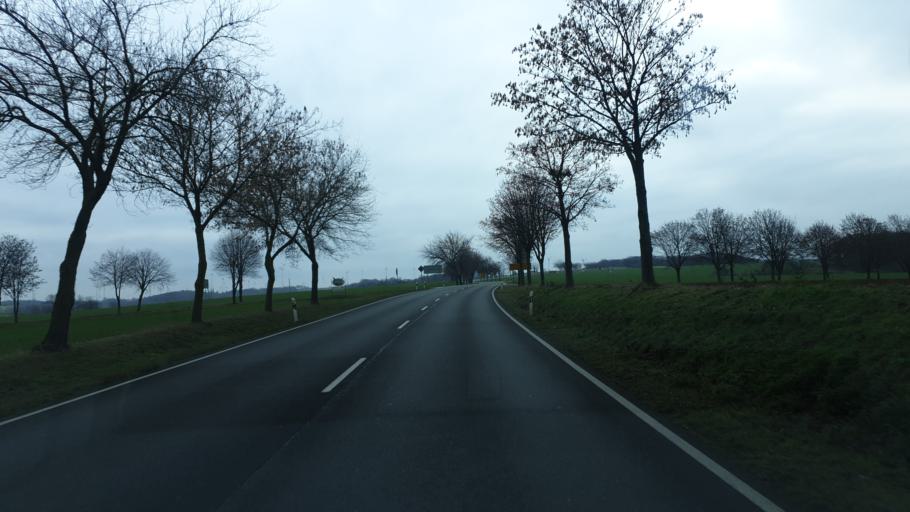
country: DE
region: Saxony-Anhalt
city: Wethau
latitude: 51.1296
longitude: 11.8846
